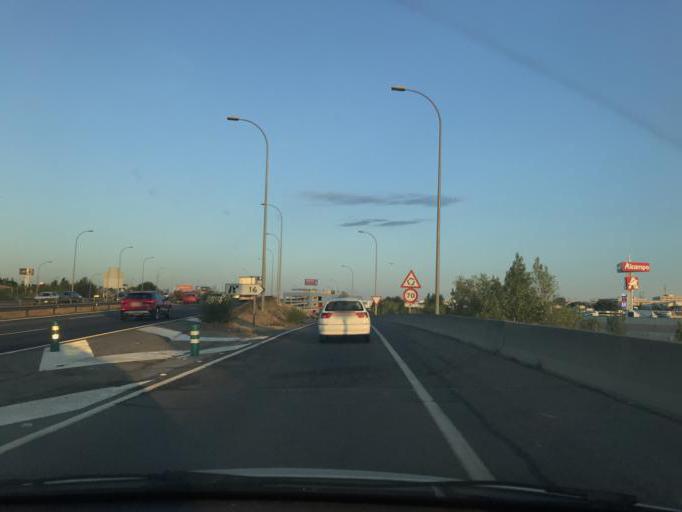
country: ES
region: Madrid
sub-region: Provincia de Madrid
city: Alcobendas
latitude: 40.5333
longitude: -3.6361
